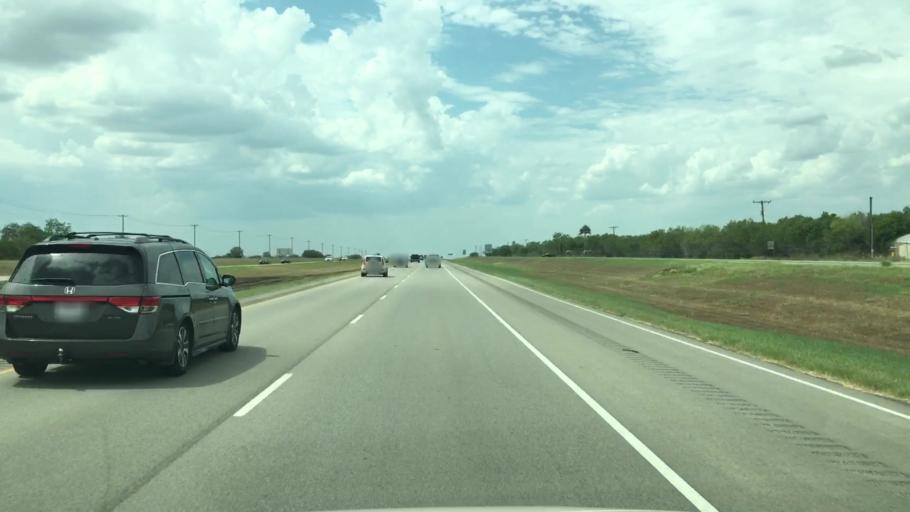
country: US
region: Texas
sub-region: Live Oak County
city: Three Rivers
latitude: 28.4967
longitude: -98.1510
